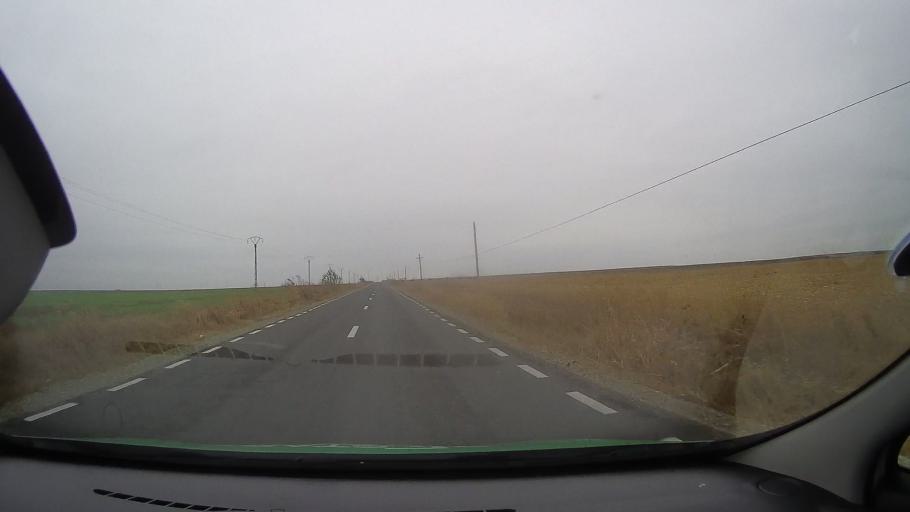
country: RO
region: Constanta
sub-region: Comuna Tortoman
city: Tortoman
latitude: 44.3521
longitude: 28.2156
